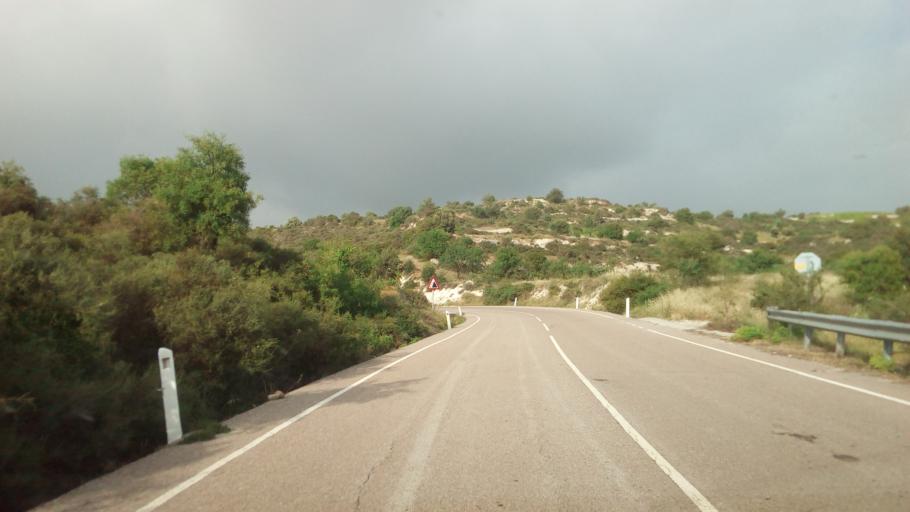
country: CY
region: Limassol
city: Pachna
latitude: 34.8256
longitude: 32.6845
